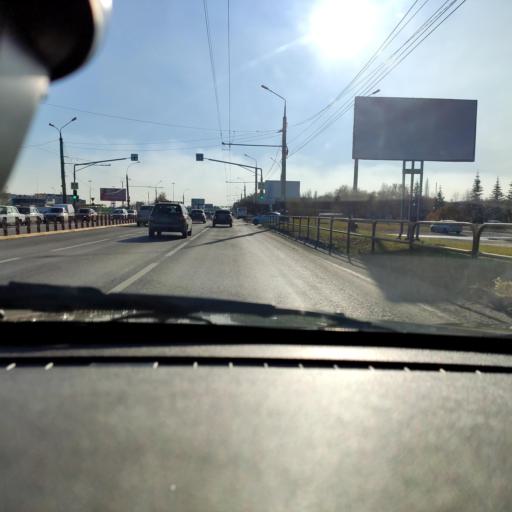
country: RU
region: Samara
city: Tol'yatti
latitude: 53.5437
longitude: 49.3826
